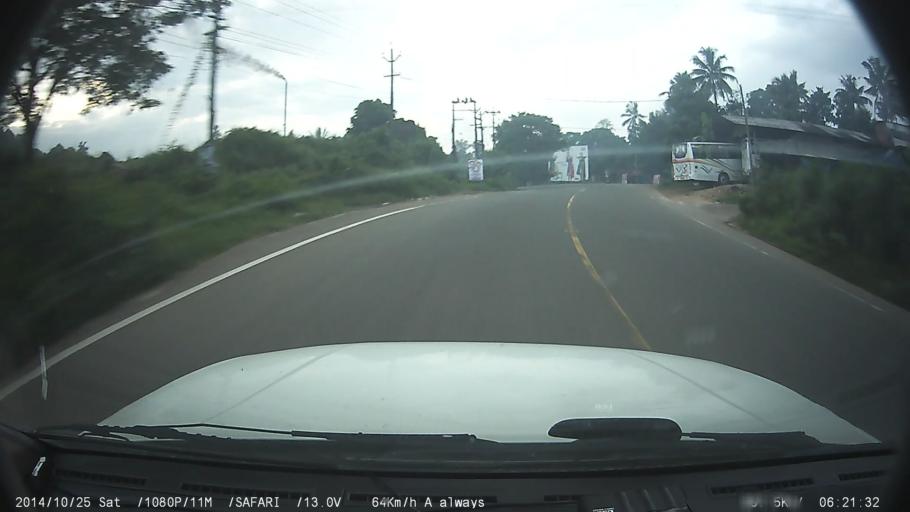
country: IN
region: Kerala
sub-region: Ernakulam
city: Perumbavoor
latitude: 10.0960
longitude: 76.4935
